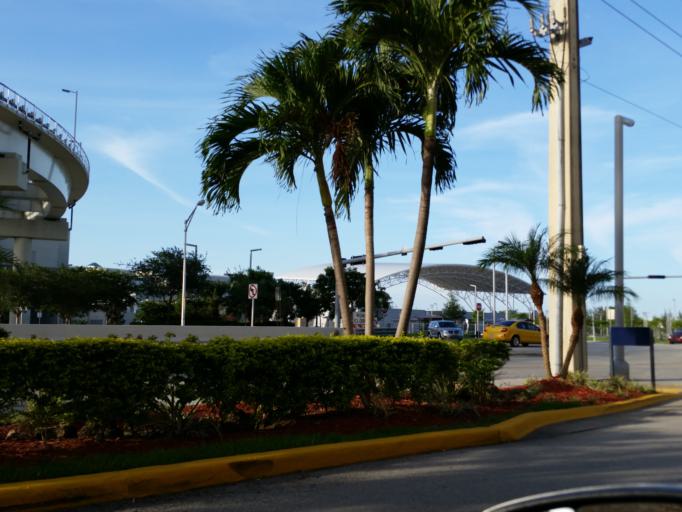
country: US
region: Florida
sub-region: Miami-Dade County
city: Brownsville
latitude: 25.7947
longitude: -80.2594
